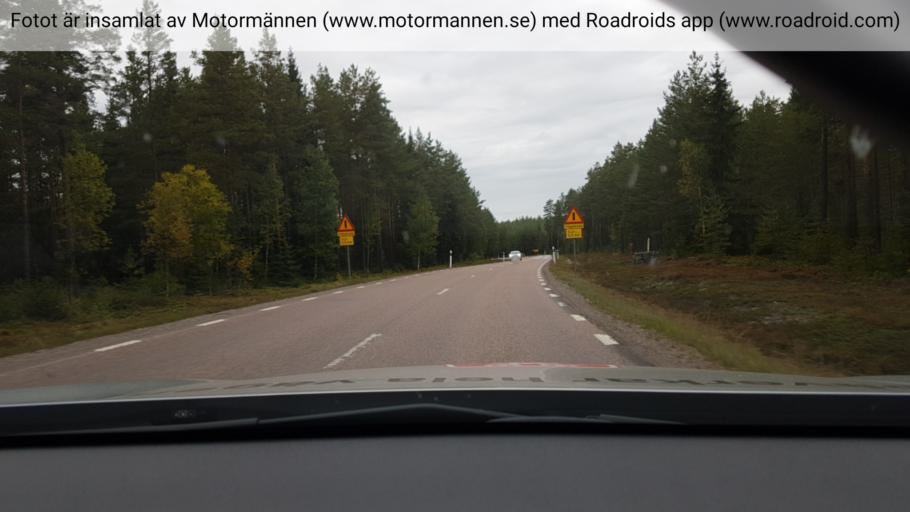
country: SE
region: Gaevleborg
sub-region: Gavle Kommun
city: Hedesunda
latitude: 60.4484
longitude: 16.9600
